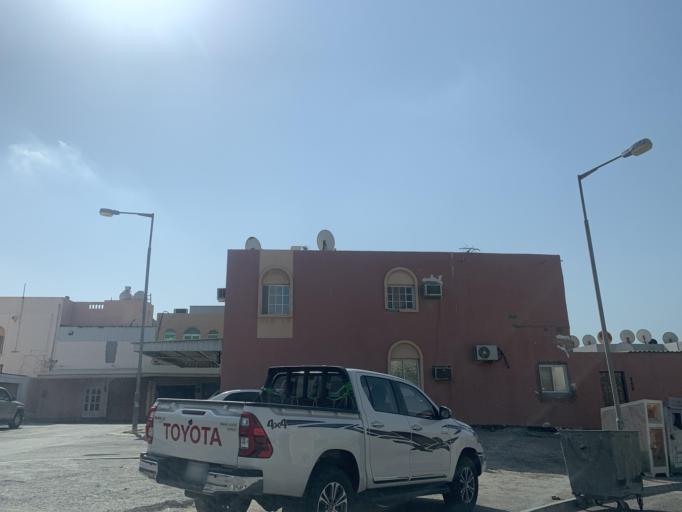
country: BH
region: Central Governorate
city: Madinat Hamad
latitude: 26.1305
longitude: 50.5013
